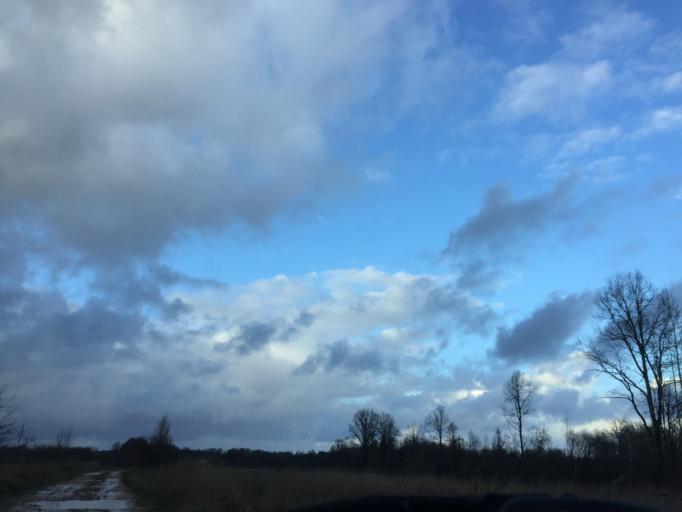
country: LV
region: Burtnieki
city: Matisi
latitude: 57.6811
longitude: 25.3066
